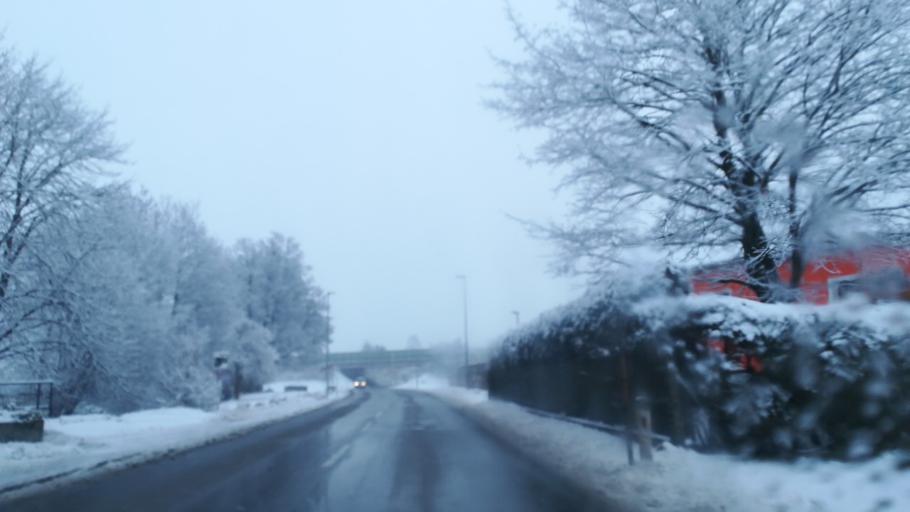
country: AT
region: Styria
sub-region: Politischer Bezirk Murtal
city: Knittelfeld
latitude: 47.2206
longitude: 14.8045
